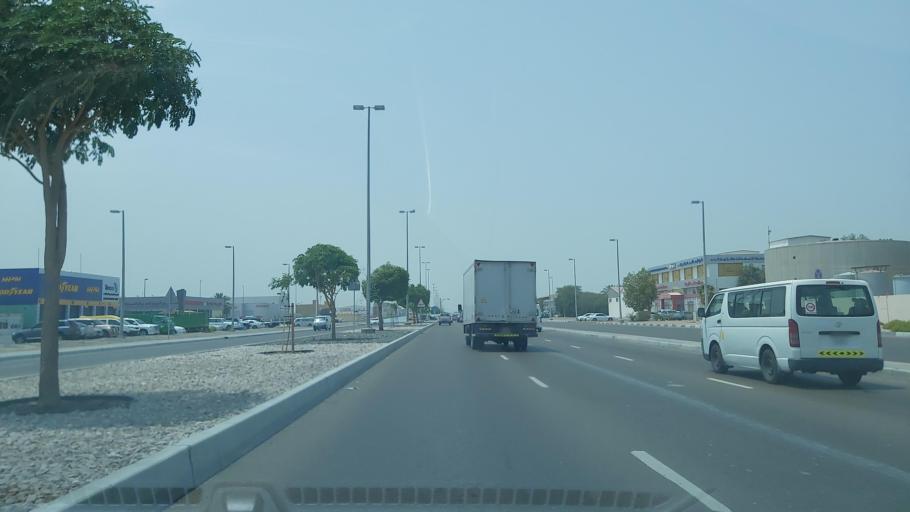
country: AE
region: Abu Dhabi
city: Abu Dhabi
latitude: 24.3824
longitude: 54.5131
